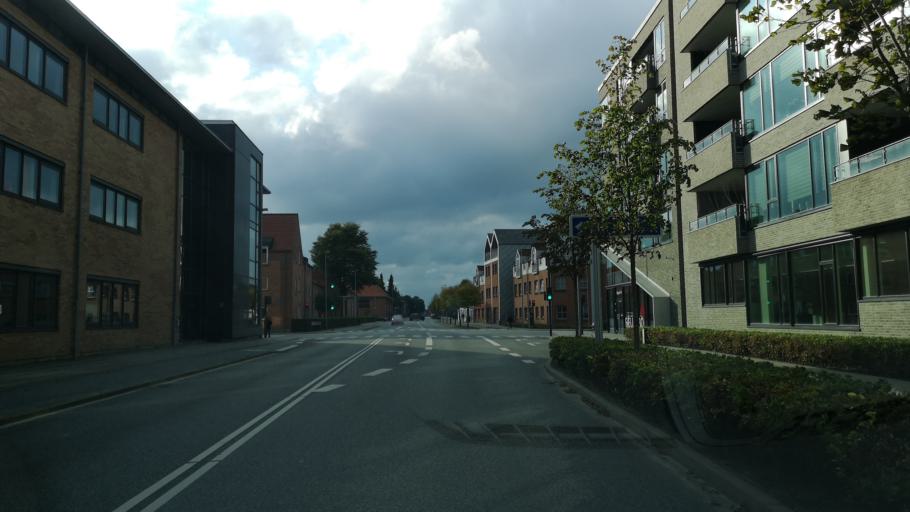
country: DK
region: Central Jutland
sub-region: Herning Kommune
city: Herning
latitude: 56.1377
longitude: 8.9736
